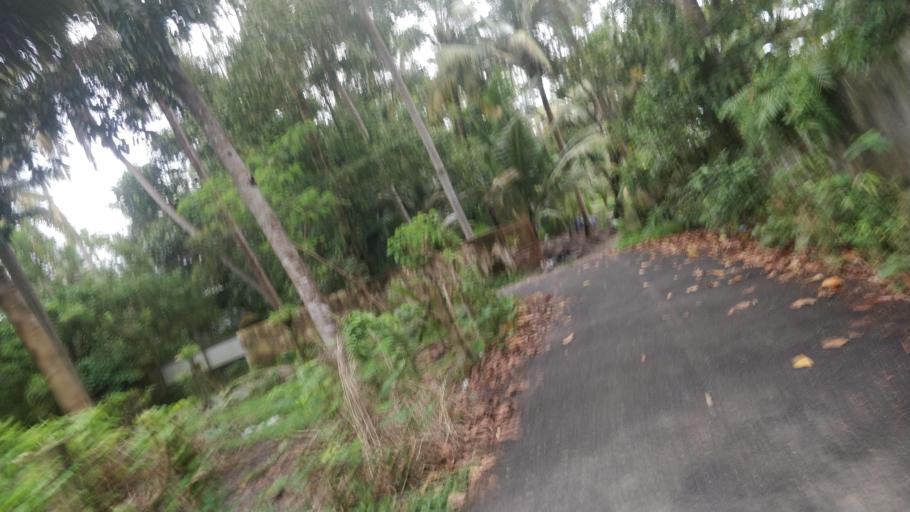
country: IN
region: Kerala
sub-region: Alappuzha
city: Shertallai
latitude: 9.6981
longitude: 76.3609
